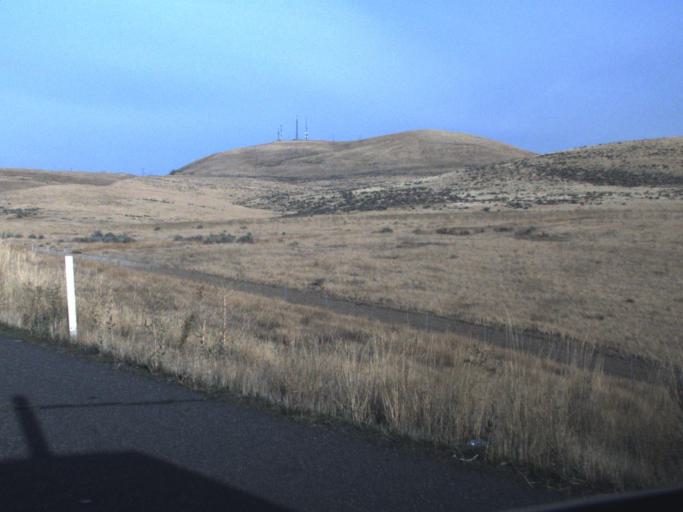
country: US
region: Oregon
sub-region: Umatilla County
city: Umatilla
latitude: 45.9781
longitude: -119.3299
